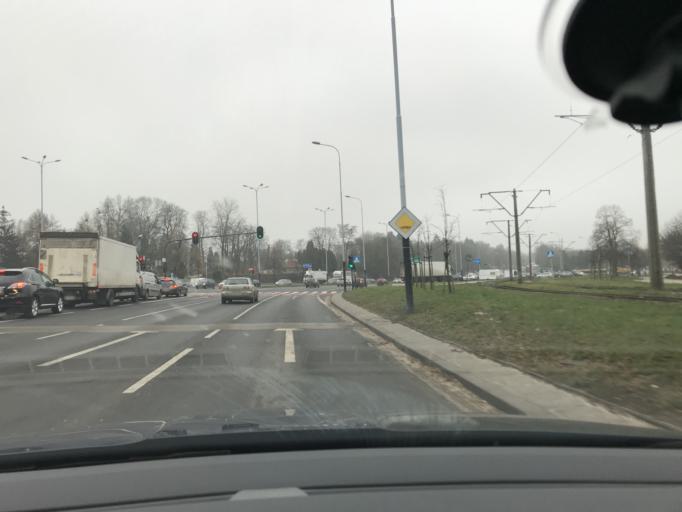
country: PL
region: Lodz Voivodeship
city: Lodz
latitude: 51.7933
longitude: 19.4884
